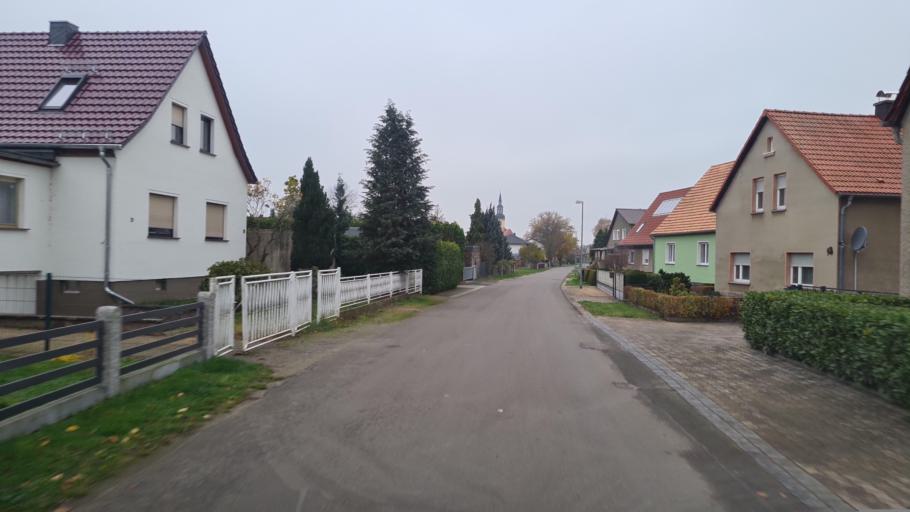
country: DE
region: Brandenburg
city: Kroppen
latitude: 51.3856
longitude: 13.8051
